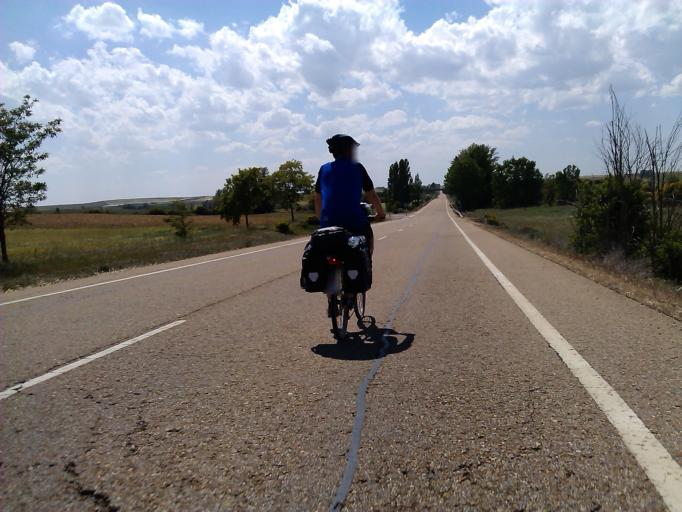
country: ES
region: Castille and Leon
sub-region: Provincia de Palencia
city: Moratinos
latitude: 42.3641
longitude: -4.8984
